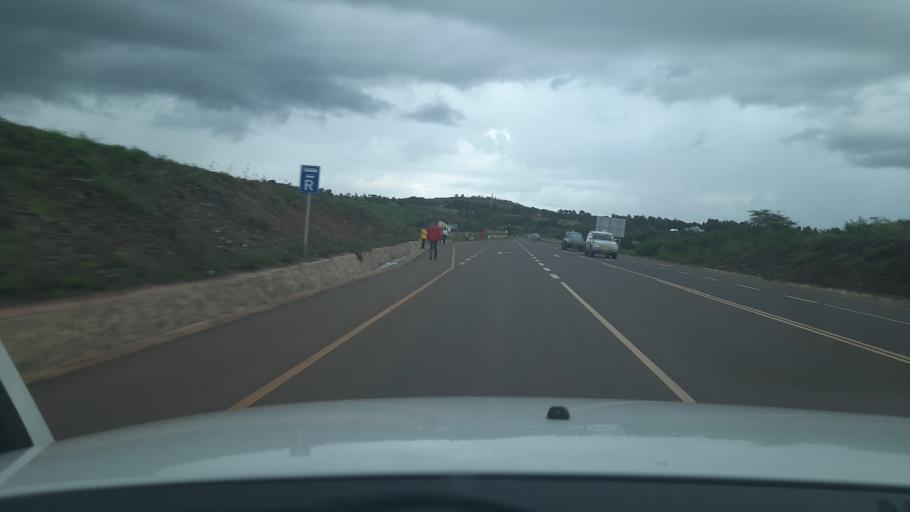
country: TZ
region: Arusha
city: Arusha
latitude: -3.4428
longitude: 36.7077
